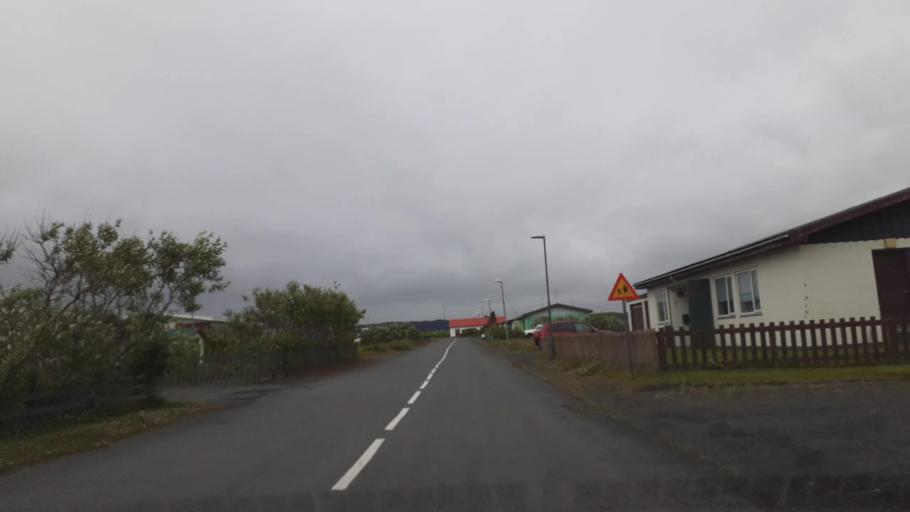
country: IS
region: Northeast
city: Husavik
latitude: 66.3029
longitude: -16.4485
